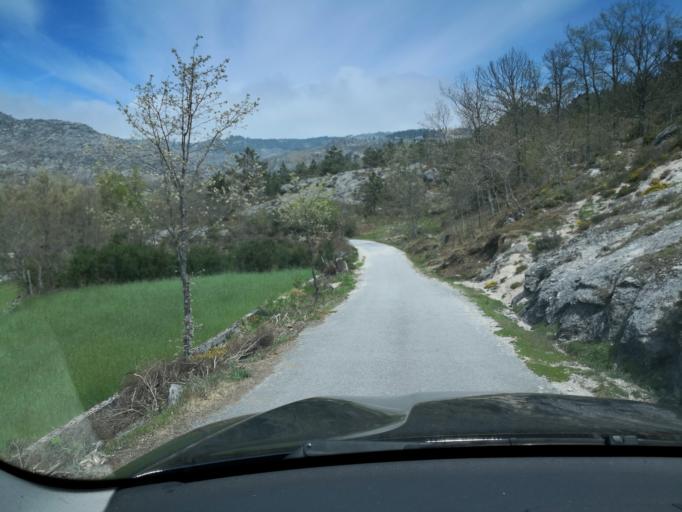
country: PT
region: Vila Real
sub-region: Vila Real
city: Vila Real
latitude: 41.3288
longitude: -7.8004
